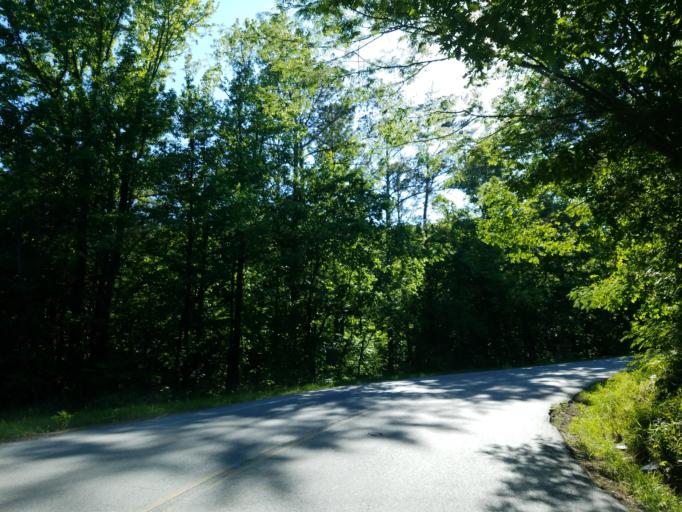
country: US
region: Georgia
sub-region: Pickens County
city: Jasper
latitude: 34.5633
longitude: -84.5185
